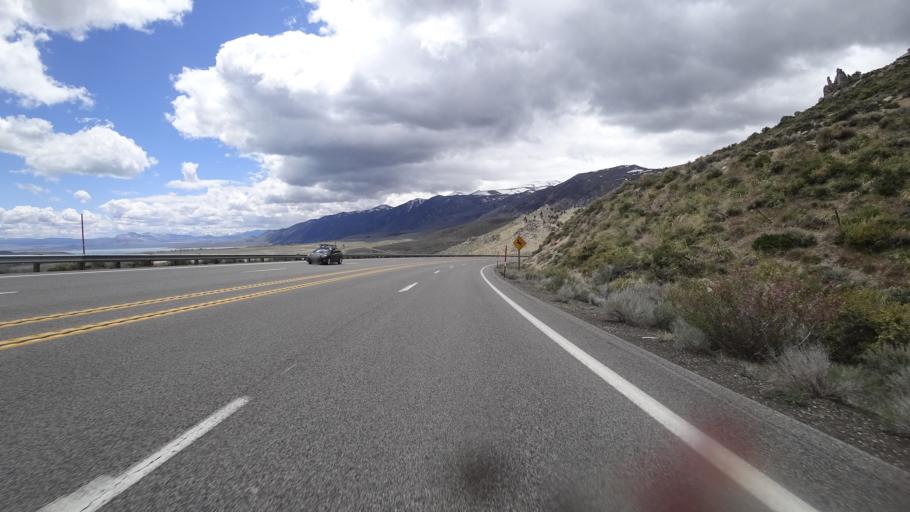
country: US
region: California
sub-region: Mono County
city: Bridgeport
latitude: 38.0738
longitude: -119.1667
